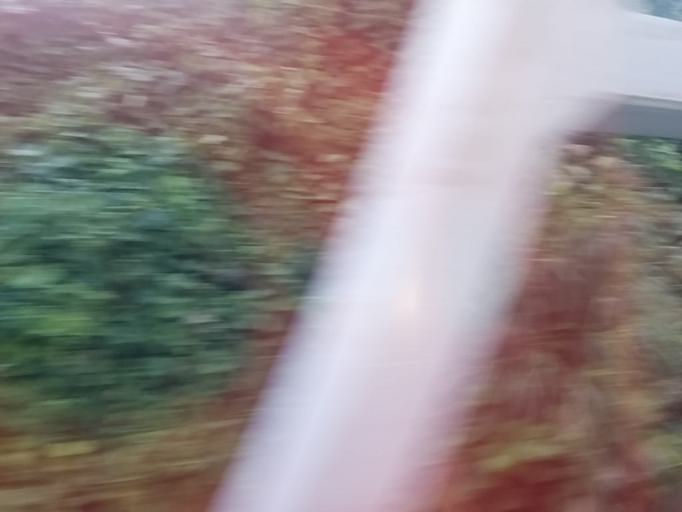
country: JP
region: Nara
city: Nara-shi
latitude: 34.7075
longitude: 135.7896
